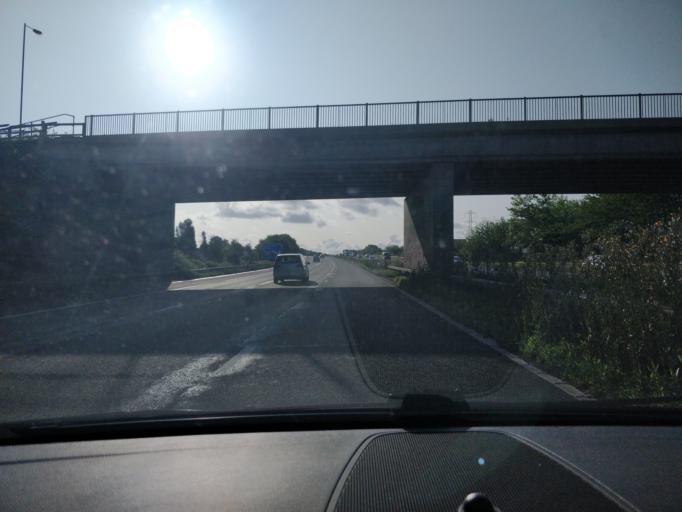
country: GB
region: England
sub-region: Sefton
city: Melling
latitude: 53.4853
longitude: -2.9278
